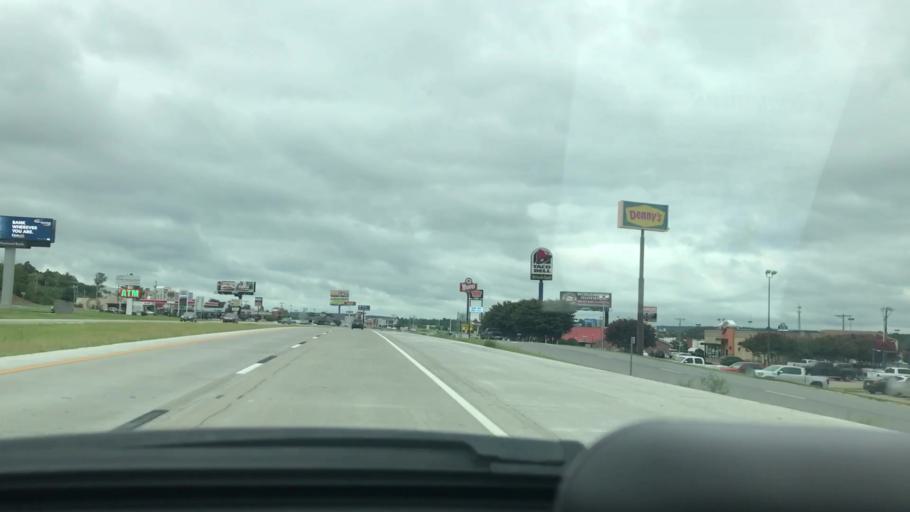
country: US
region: Oklahoma
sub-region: Pittsburg County
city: McAlester
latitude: 34.9159
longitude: -95.7452
